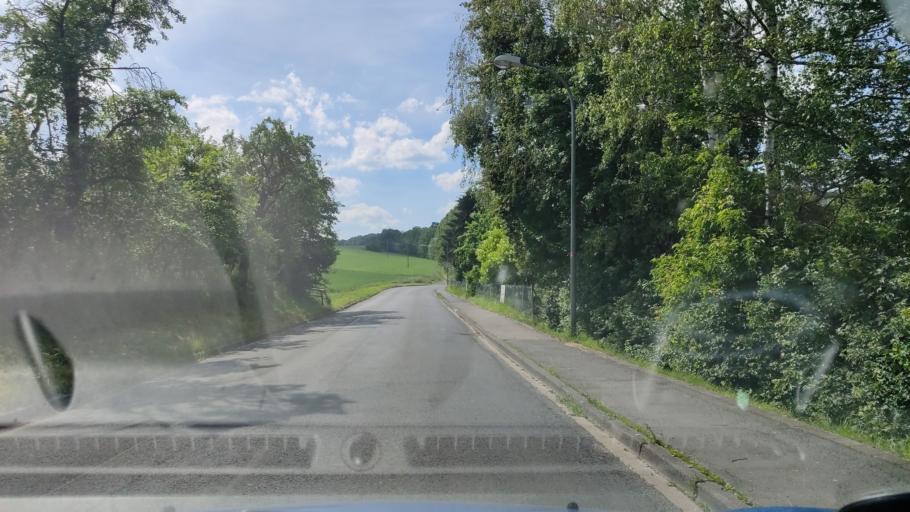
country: DE
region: Lower Saxony
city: Rosdorf
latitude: 51.5339
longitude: 9.8523
